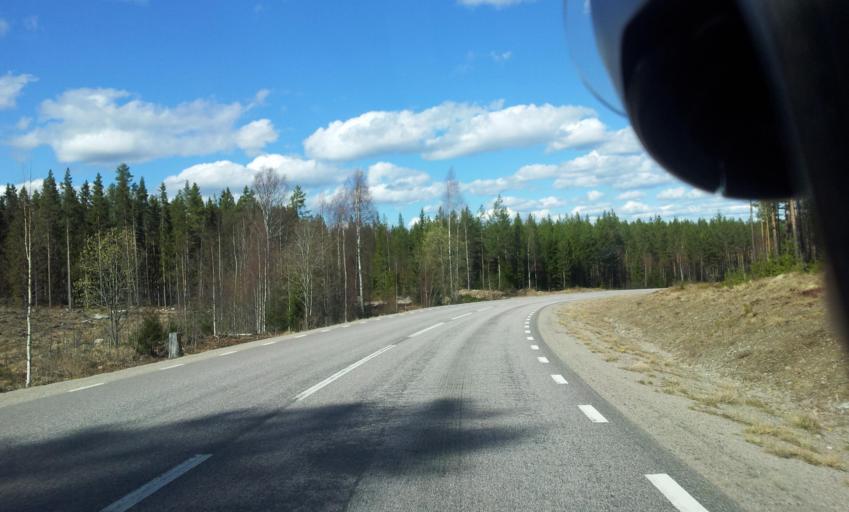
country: SE
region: Gaevleborg
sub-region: Bollnas Kommun
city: Vittsjo
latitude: 61.1457
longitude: 15.8853
